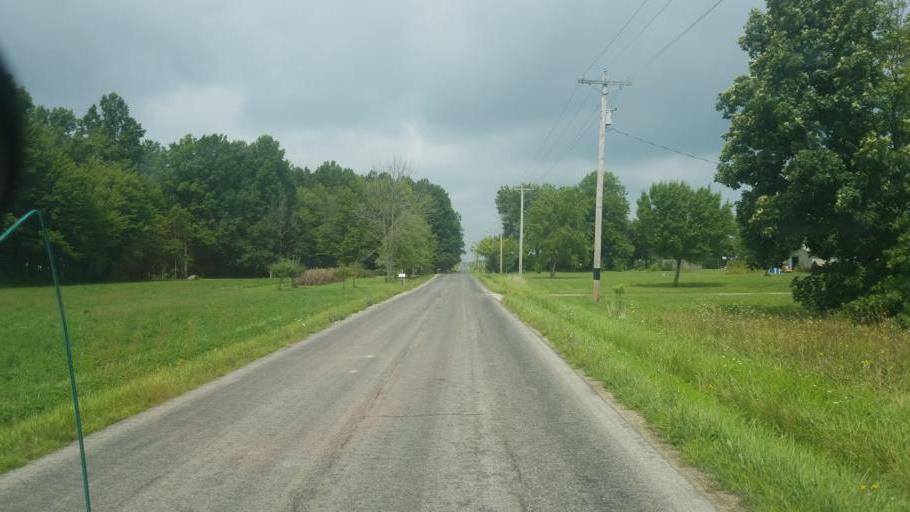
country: US
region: Ohio
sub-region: Huron County
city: Greenwich
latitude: 40.9890
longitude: -82.4777
